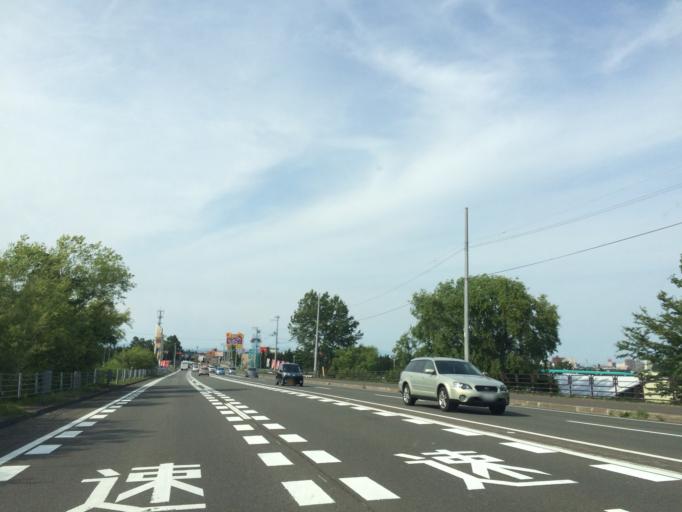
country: JP
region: Hokkaido
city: Ebetsu
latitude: 43.0836
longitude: 141.5153
